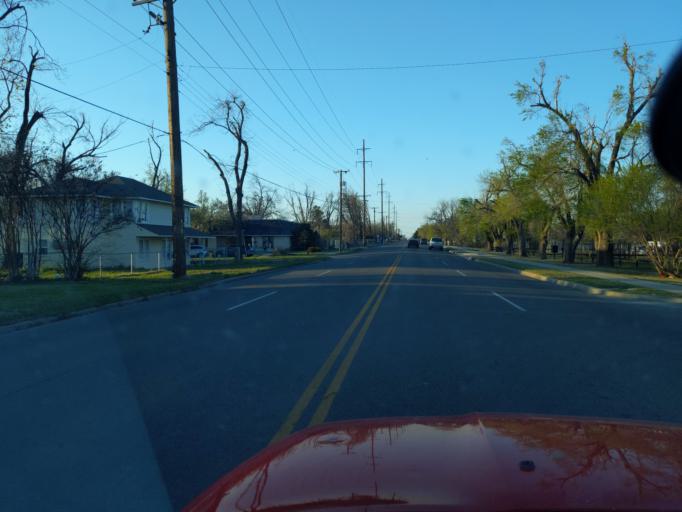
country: US
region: Oklahoma
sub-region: Oklahoma County
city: Oklahoma City
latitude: 35.4097
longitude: -97.5213
